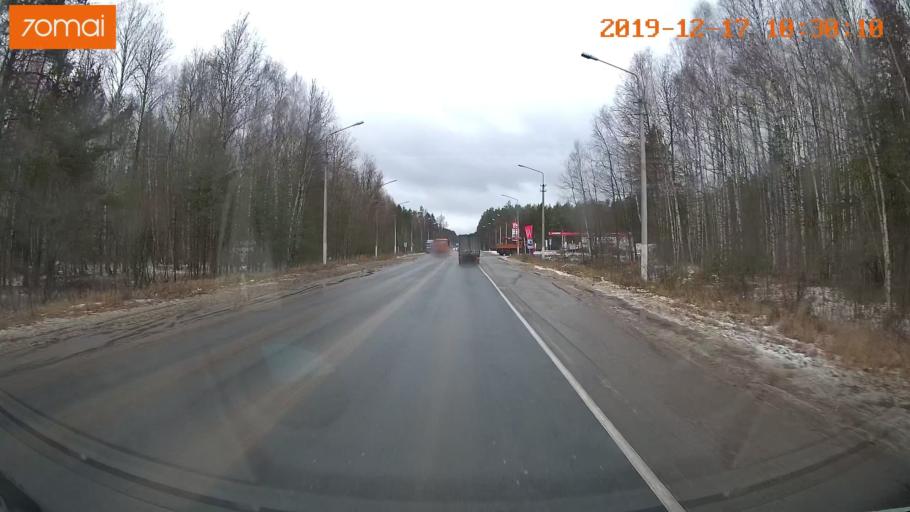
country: RU
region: Vladimir
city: Gus'-Khrustal'nyy
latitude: 55.6446
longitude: 40.7116
